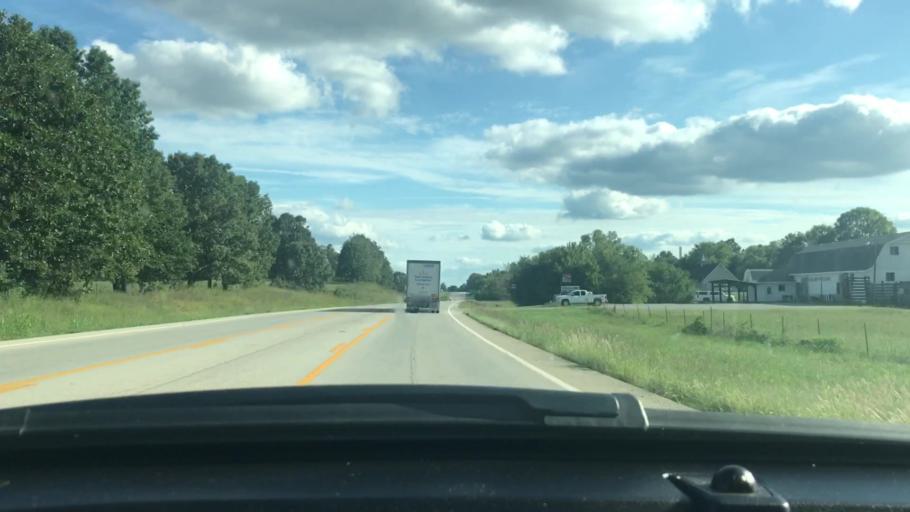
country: US
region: Missouri
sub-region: Oregon County
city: Thayer
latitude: 36.6026
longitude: -91.6440
